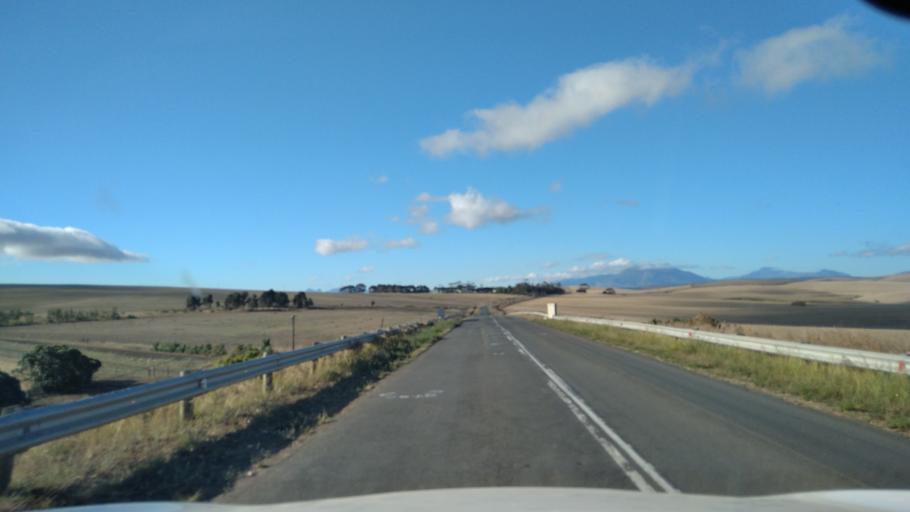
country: ZA
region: Western Cape
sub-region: Overberg District Municipality
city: Caledon
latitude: -34.2119
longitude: 19.2728
